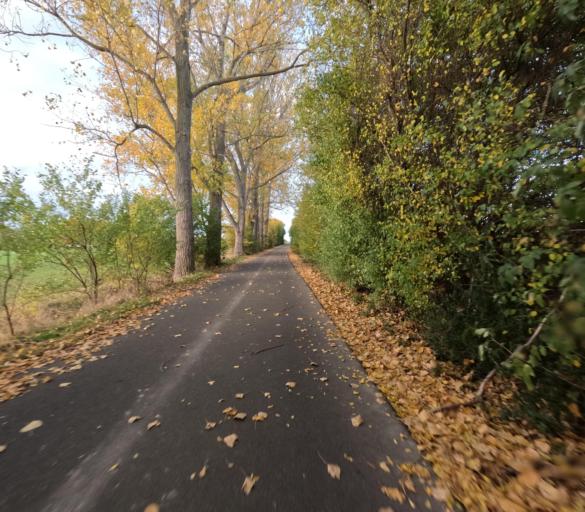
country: DE
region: Saxony
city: Grimma
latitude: 51.2511
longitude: 12.6947
